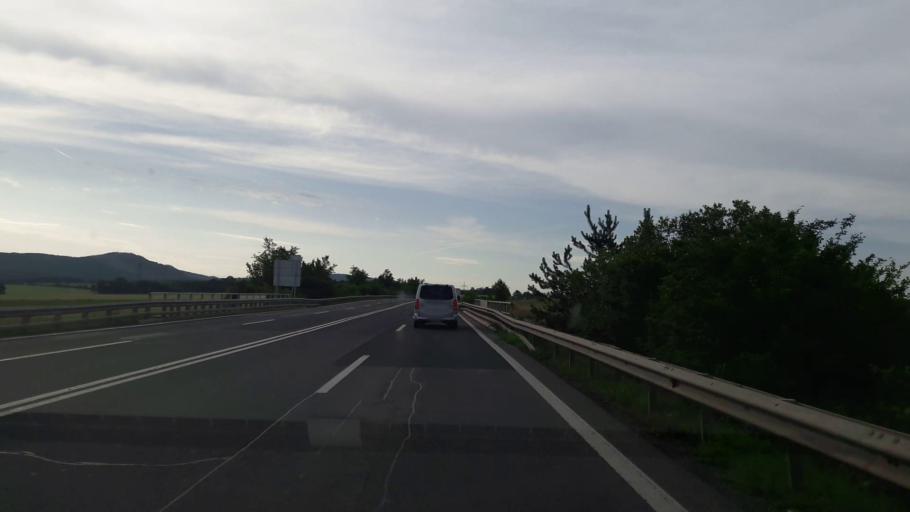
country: AT
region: Burgenland
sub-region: Politischer Bezirk Oberpullendorf
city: Markt Sankt Martin
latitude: 47.5417
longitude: 16.4259
